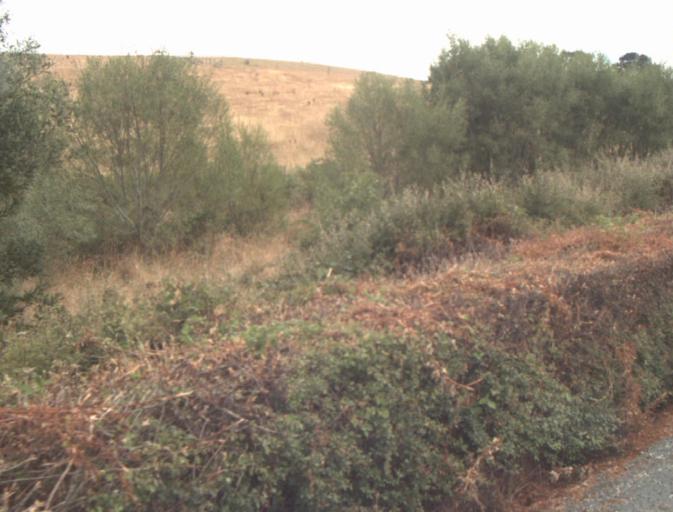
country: AU
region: Tasmania
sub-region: Northern Midlands
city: Evandale
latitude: -41.5257
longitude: 147.2467
